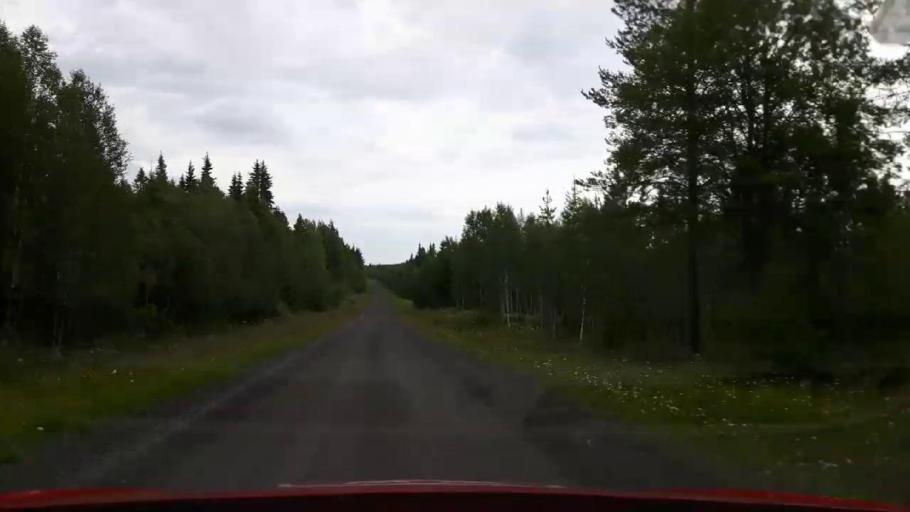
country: SE
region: Jaemtland
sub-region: OEstersunds Kommun
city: Lit
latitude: 63.3946
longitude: 15.2204
